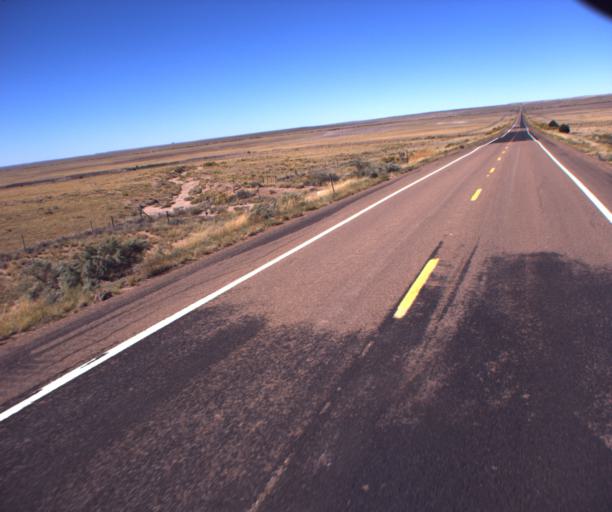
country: US
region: Arizona
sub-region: Navajo County
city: Snowflake
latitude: 34.7199
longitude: -109.7719
